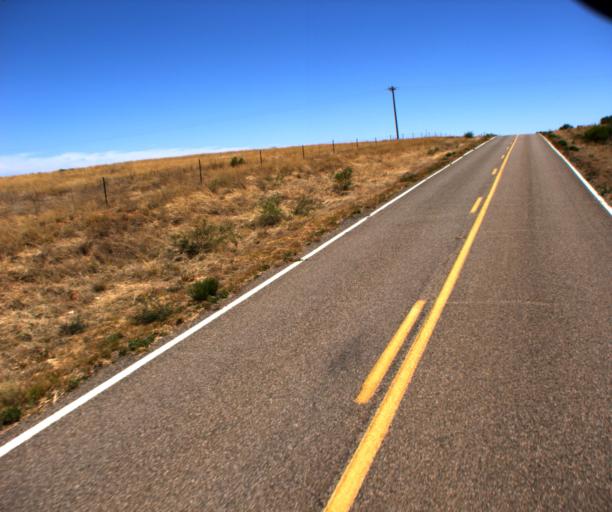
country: US
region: Arizona
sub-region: Pima County
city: Sells
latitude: 31.5860
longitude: -111.5332
